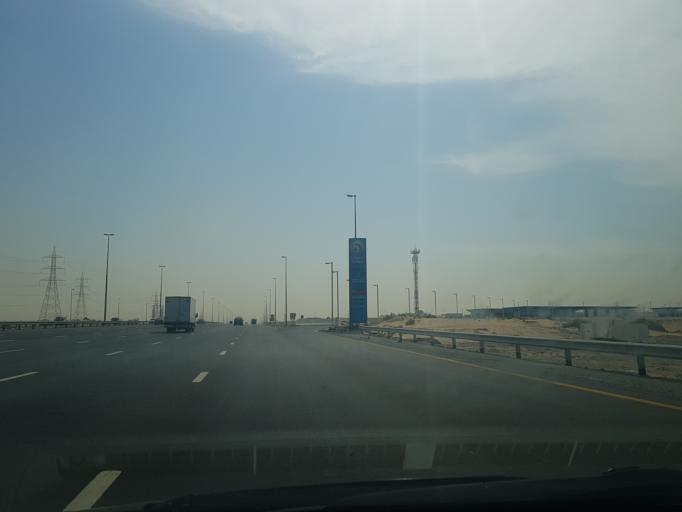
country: AE
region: Ash Shariqah
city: Sharjah
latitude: 25.2572
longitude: 55.5747
